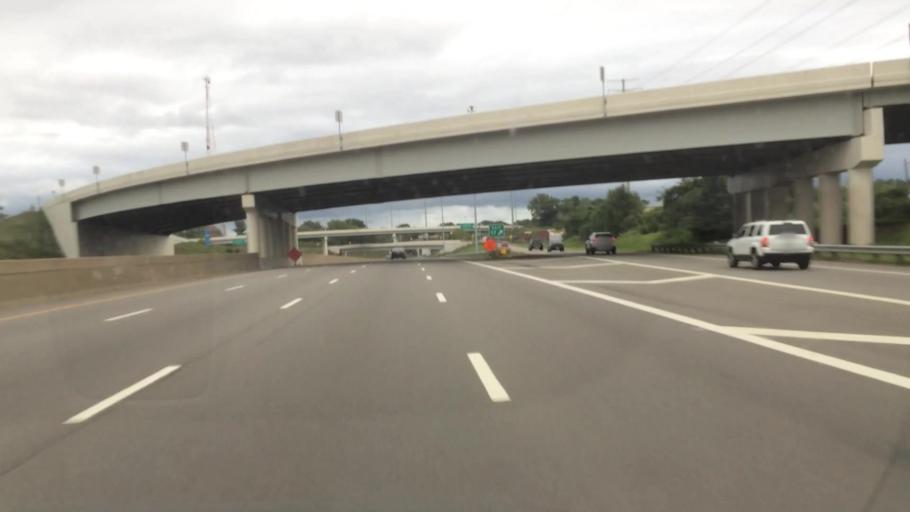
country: US
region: Ohio
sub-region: Cuyahoga County
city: Brooklyn Heights
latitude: 41.4207
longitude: -81.6909
